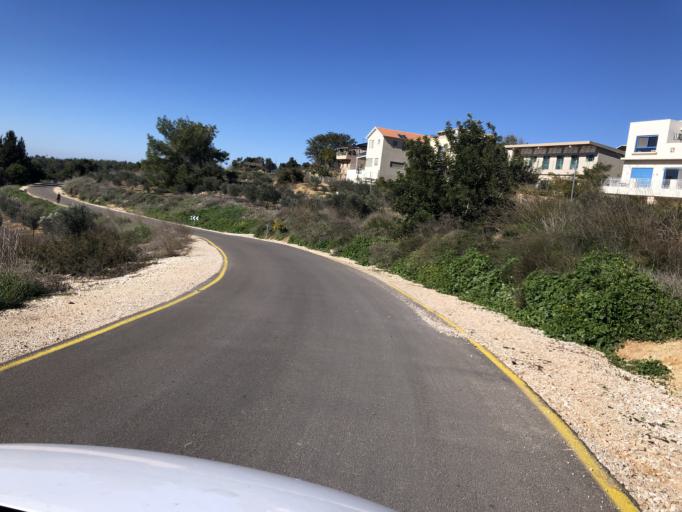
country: IL
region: Jerusalem
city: Zur Hadassa
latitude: 31.7450
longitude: 35.0520
